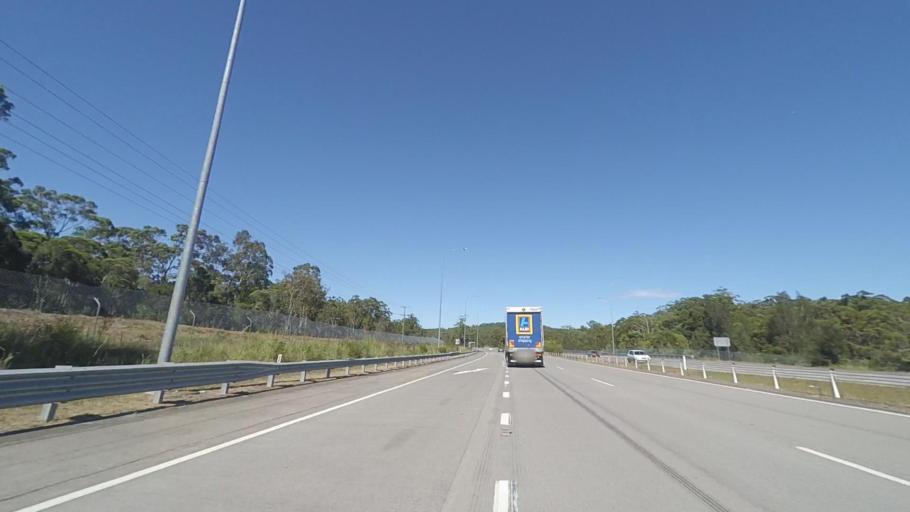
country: AU
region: New South Wales
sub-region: Port Stephens Shire
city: Port Stephens
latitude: -32.6112
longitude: 152.0873
